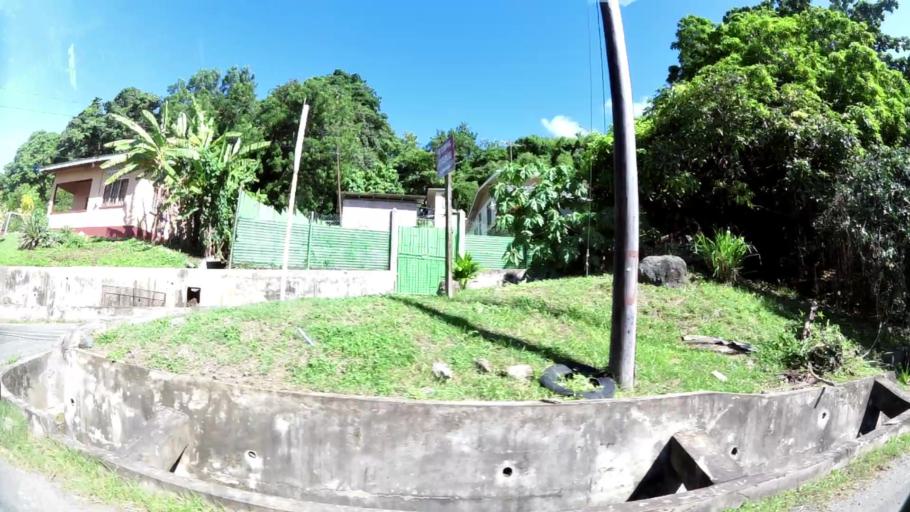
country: TT
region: Tobago
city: Scarborough
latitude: 11.1744
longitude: -60.7278
